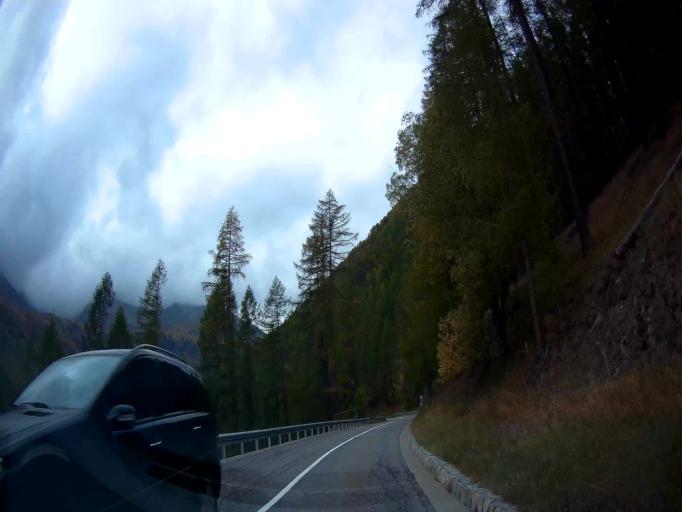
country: IT
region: Trentino-Alto Adige
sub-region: Bolzano
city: Senales
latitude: 46.7383
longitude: 10.8266
